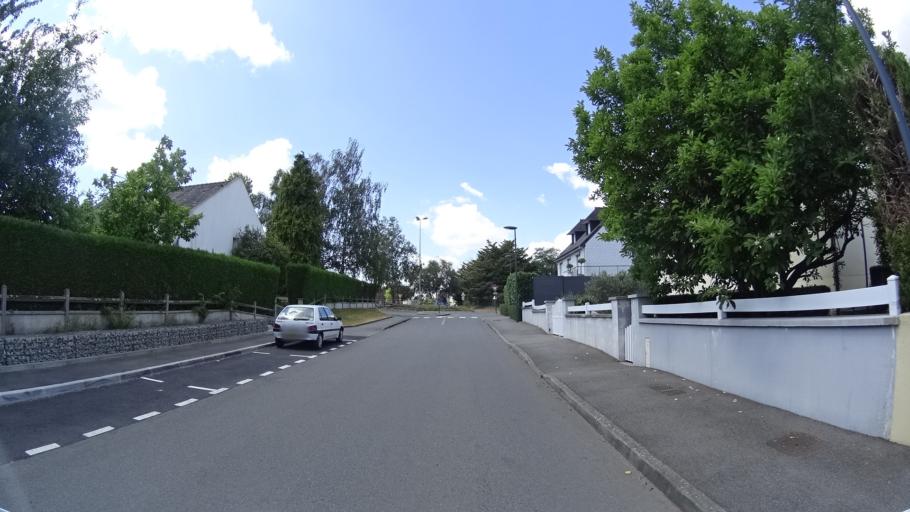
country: FR
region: Brittany
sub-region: Departement d'Ille-et-Vilaine
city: Noyal-sur-Vilaine
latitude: 48.1167
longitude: -1.5314
